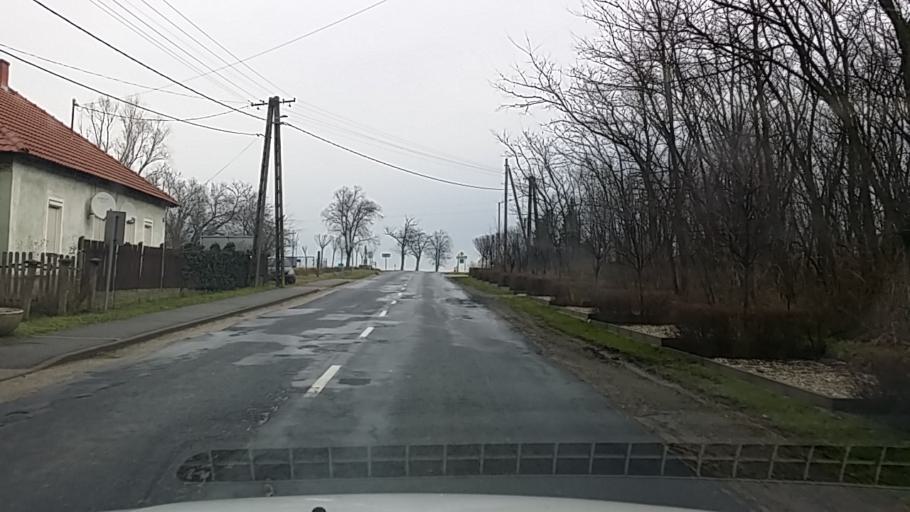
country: HU
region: Vas
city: Celldomolk
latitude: 47.2735
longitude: 17.3100
